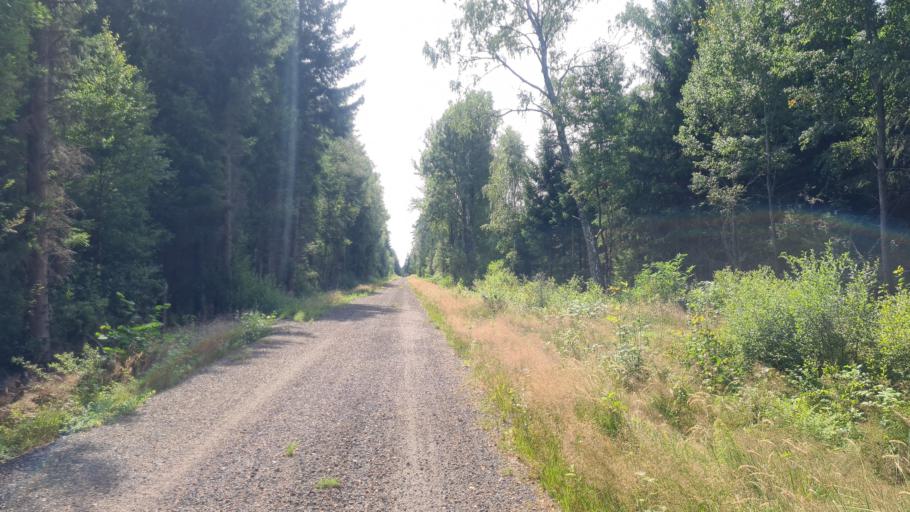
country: SE
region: Kronoberg
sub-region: Ljungby Kommun
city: Lagan
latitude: 56.9650
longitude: 13.9532
